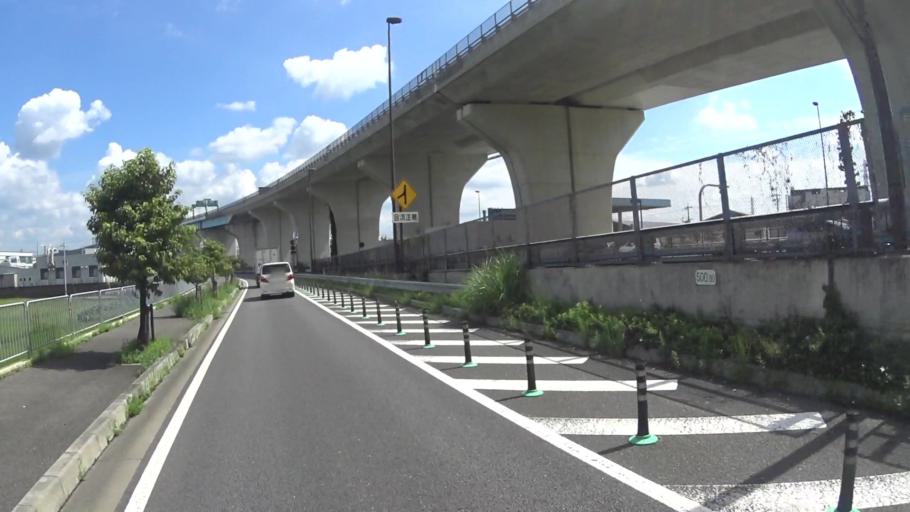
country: JP
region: Kyoto
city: Yawata
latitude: 34.8987
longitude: 135.7413
